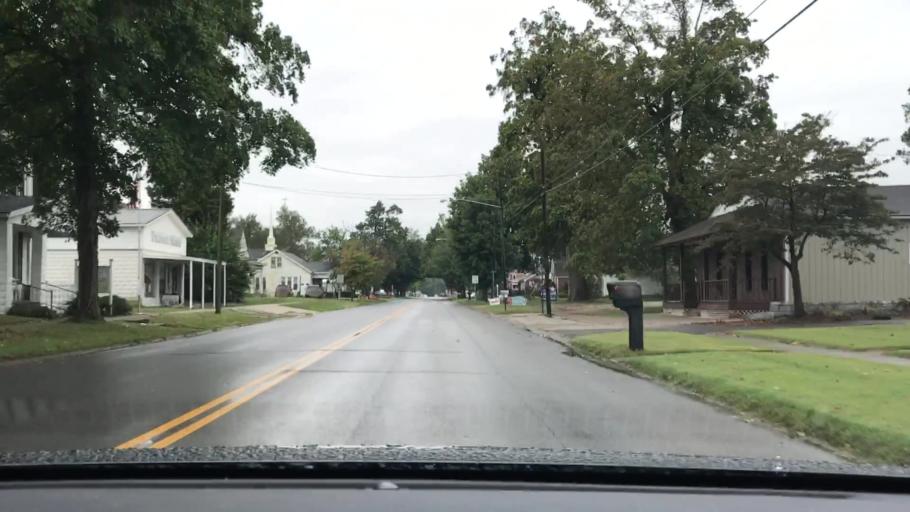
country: US
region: Kentucky
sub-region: McLean County
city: Calhoun
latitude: 37.5411
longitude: -87.2585
